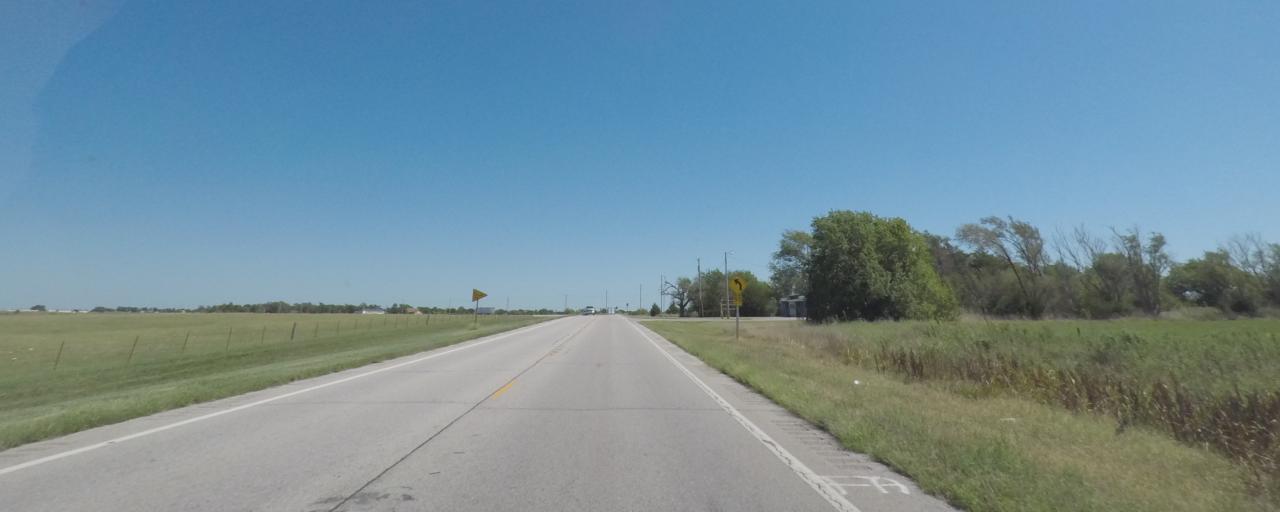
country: US
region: Kansas
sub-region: Sumner County
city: Wellington
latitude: 37.3056
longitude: -97.3874
